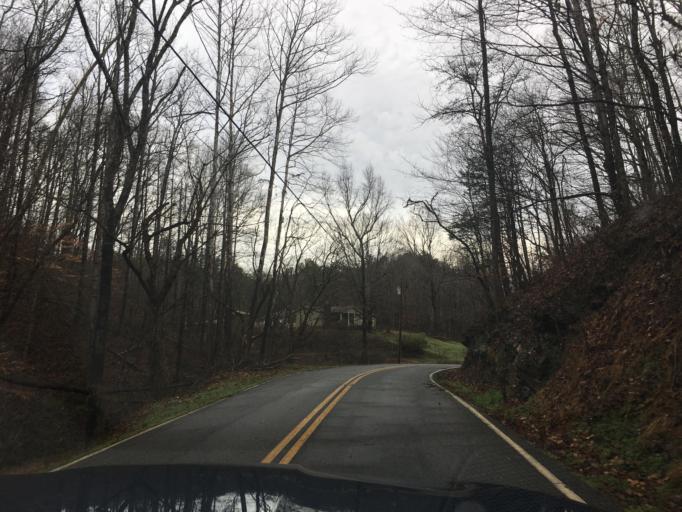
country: US
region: Tennessee
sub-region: McMinn County
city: Englewood
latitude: 35.3716
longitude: -84.4359
